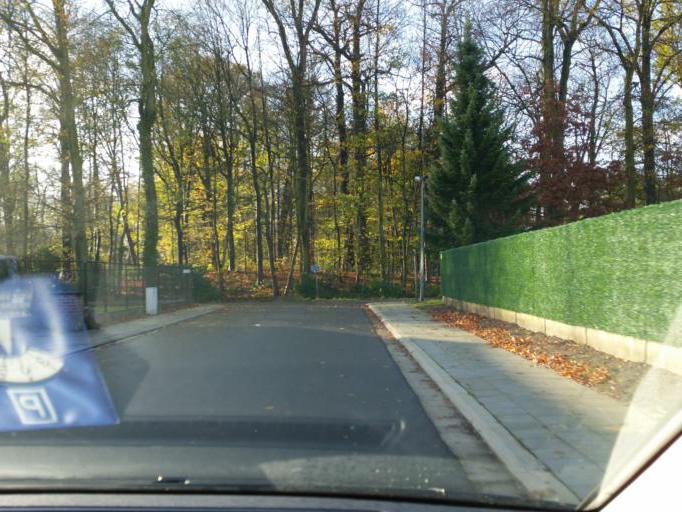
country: BE
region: Flanders
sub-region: Provincie Vlaams-Brabant
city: Zemst
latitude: 50.9620
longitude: 4.4467
